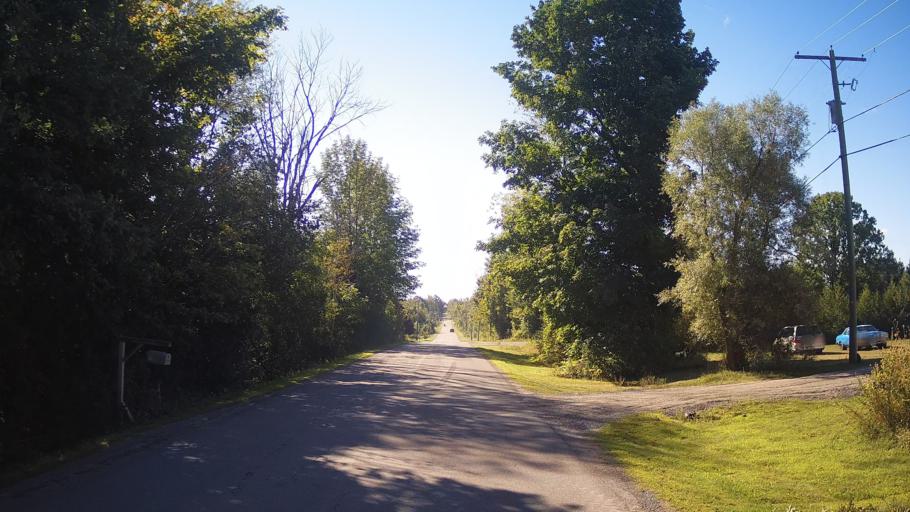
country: CA
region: Ontario
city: Prescott
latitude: 45.0109
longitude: -75.6089
